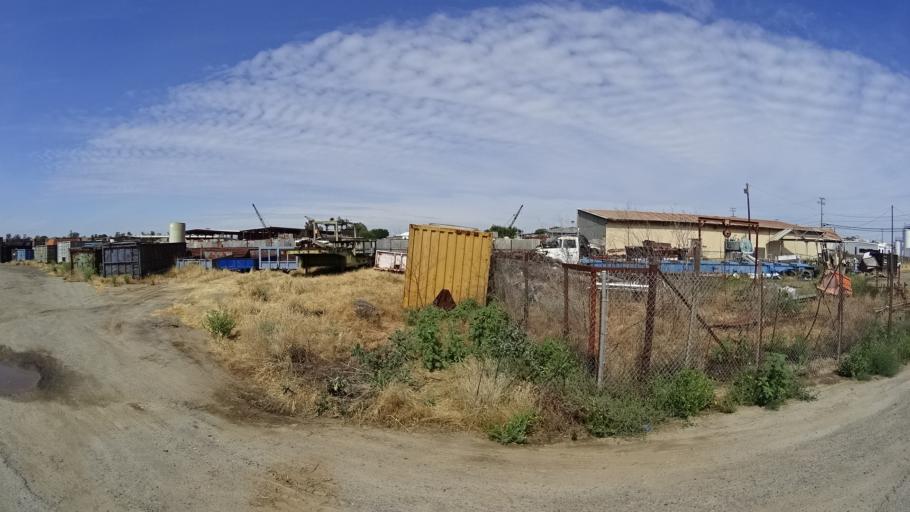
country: US
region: California
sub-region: Kings County
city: Hanford
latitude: 36.3270
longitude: -119.6213
